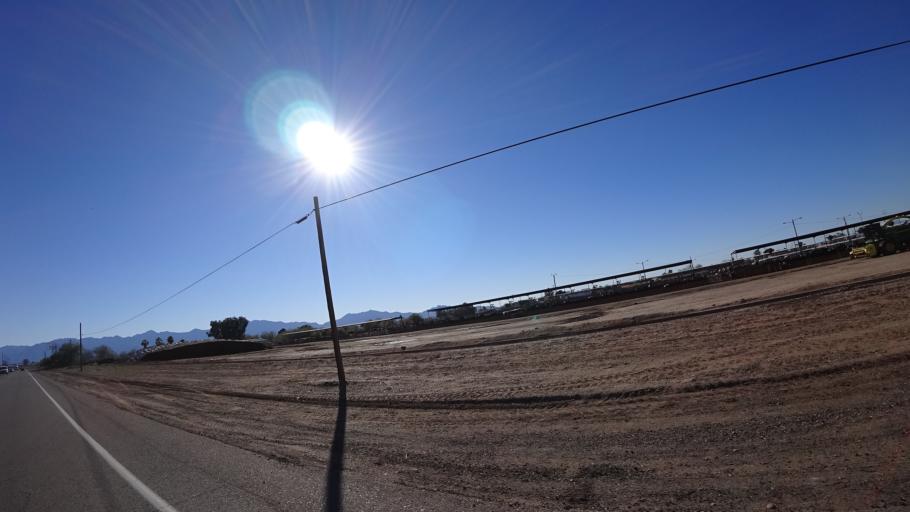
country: US
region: Arizona
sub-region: Maricopa County
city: Laveen
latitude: 33.4058
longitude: -112.2041
